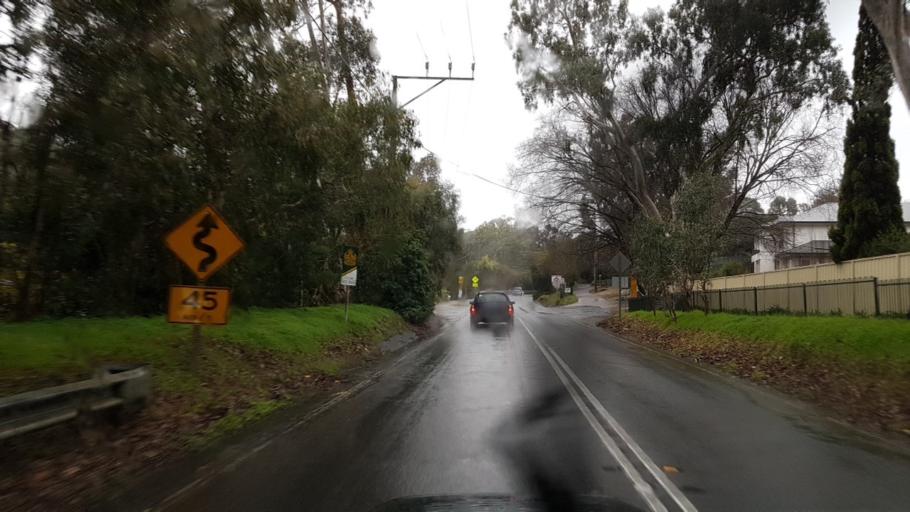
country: AU
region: South Australia
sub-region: Mitcham
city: Blackwood
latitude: -35.0347
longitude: 138.6249
